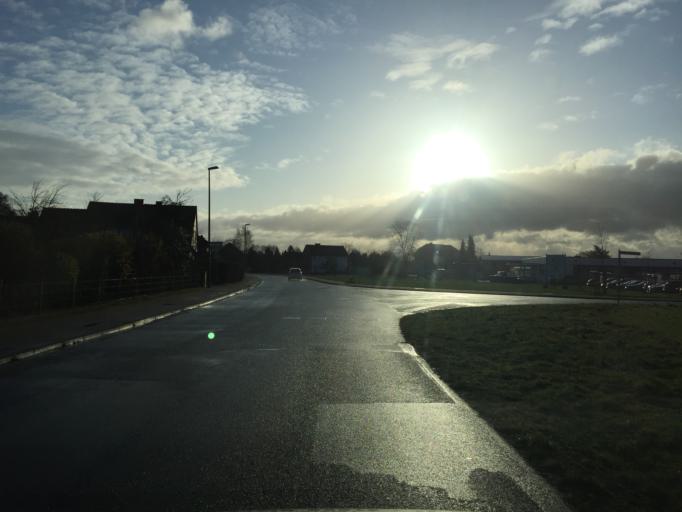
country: DE
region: Lower Saxony
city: Steyerberg
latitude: 52.5639
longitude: 9.0152
